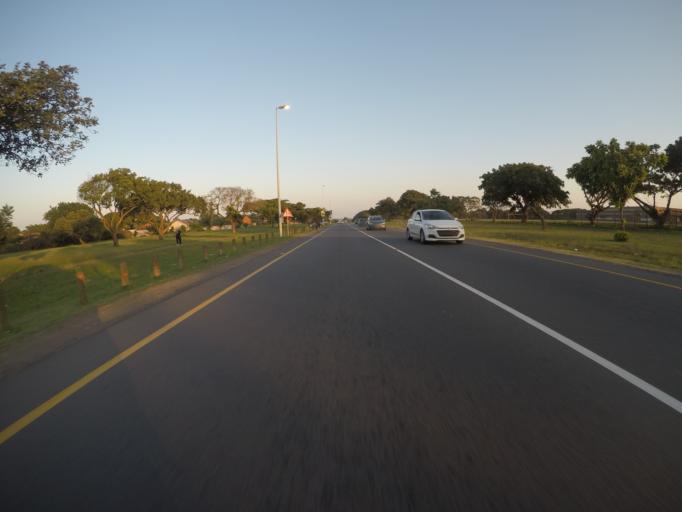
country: ZA
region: KwaZulu-Natal
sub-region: uThungulu District Municipality
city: Richards Bay
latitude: -28.7590
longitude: 32.0587
